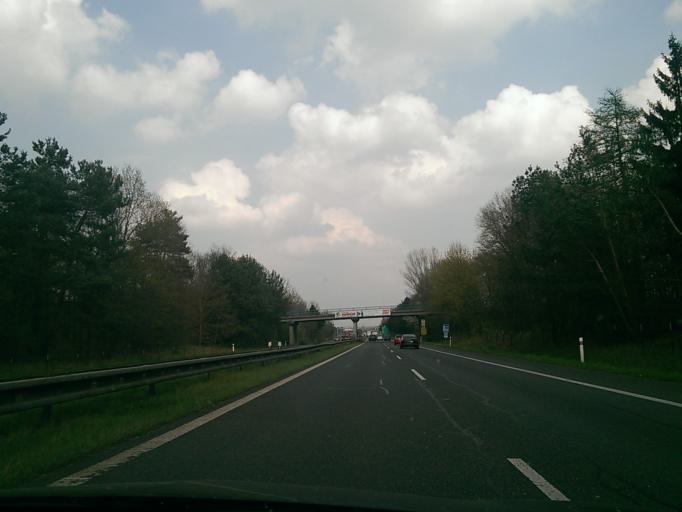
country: CZ
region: Central Bohemia
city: Benatky nad Jizerou
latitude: 50.2734
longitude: 14.8151
